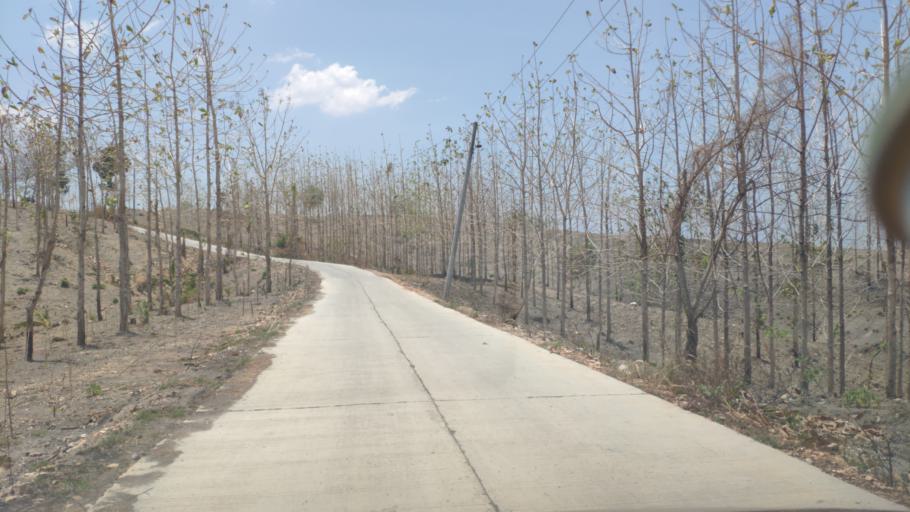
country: ID
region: Central Java
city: Temulus
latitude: -7.2847
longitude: 111.3735
